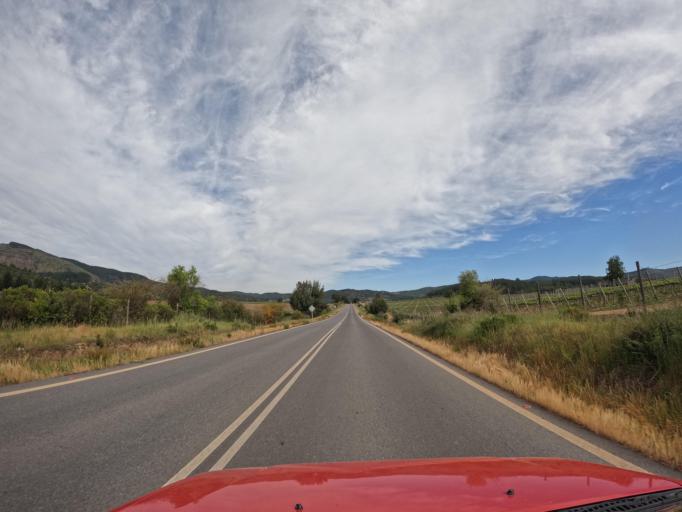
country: CL
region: Maule
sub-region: Provincia de Talca
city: Talca
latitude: -35.3372
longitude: -71.9229
